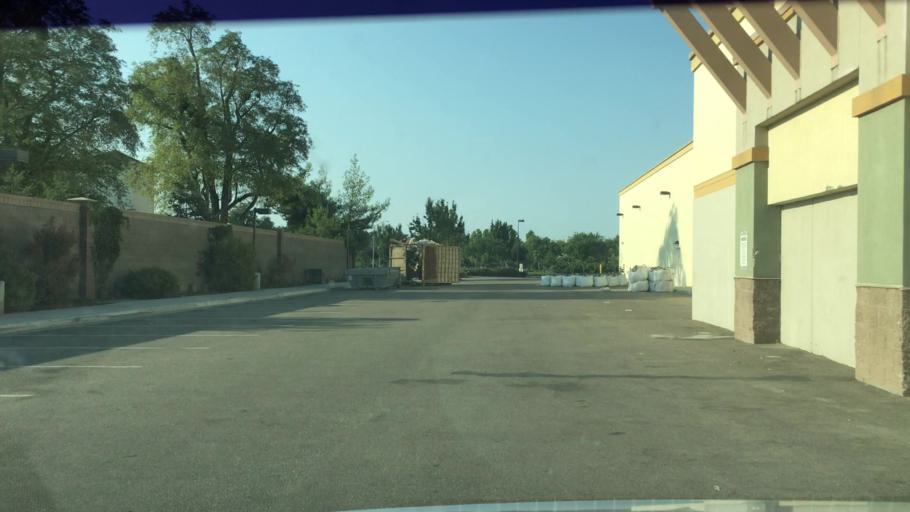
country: US
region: California
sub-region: San Joaquin County
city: Lodi
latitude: 38.0979
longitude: -121.2614
